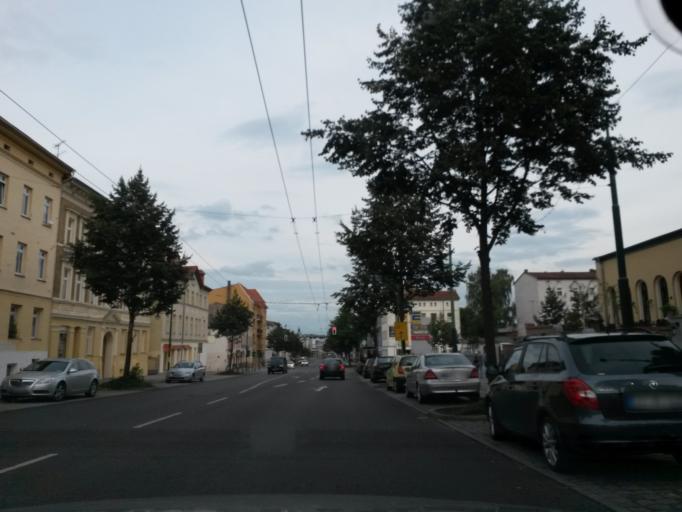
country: DE
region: Brandenburg
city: Eberswalde
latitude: 52.8336
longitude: 13.8071
